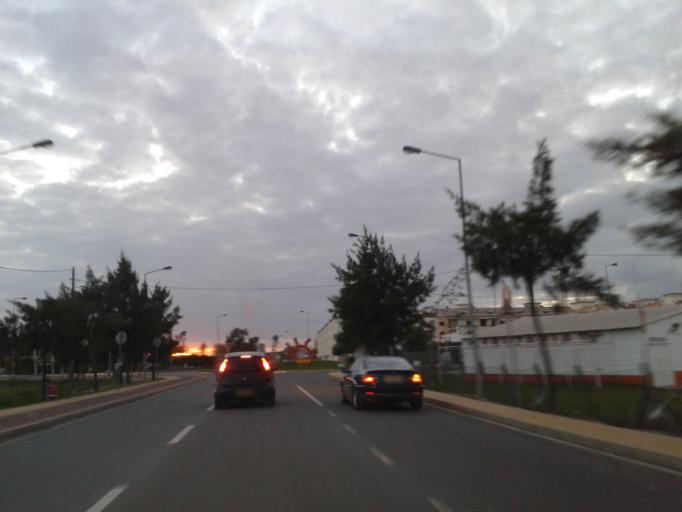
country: PT
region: Faro
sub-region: Vila Real de Santo Antonio
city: Monte Gordo
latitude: 37.1874
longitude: -7.4498
